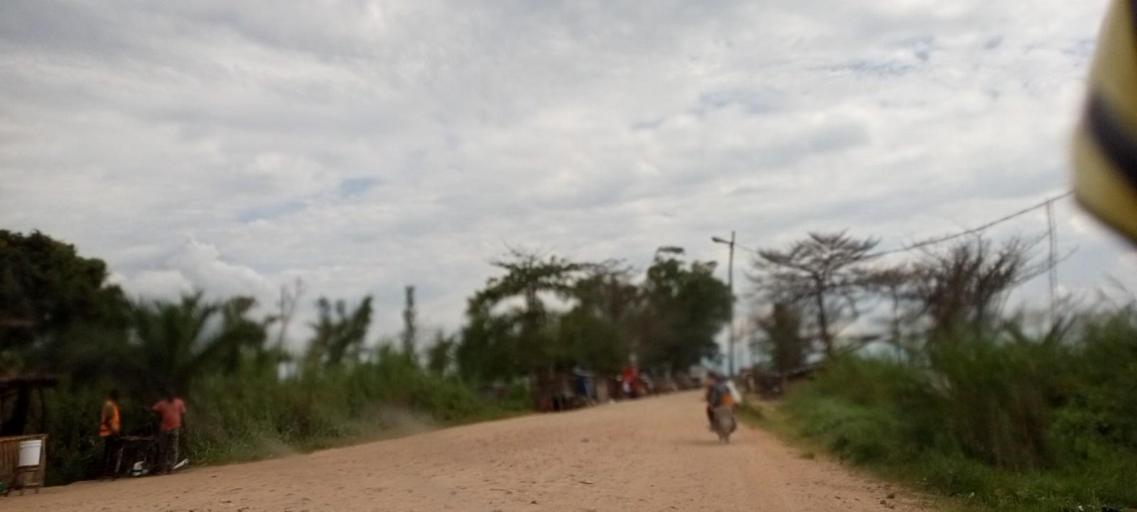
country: CD
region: South Kivu
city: Uvira
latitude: -3.3401
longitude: 29.2015
